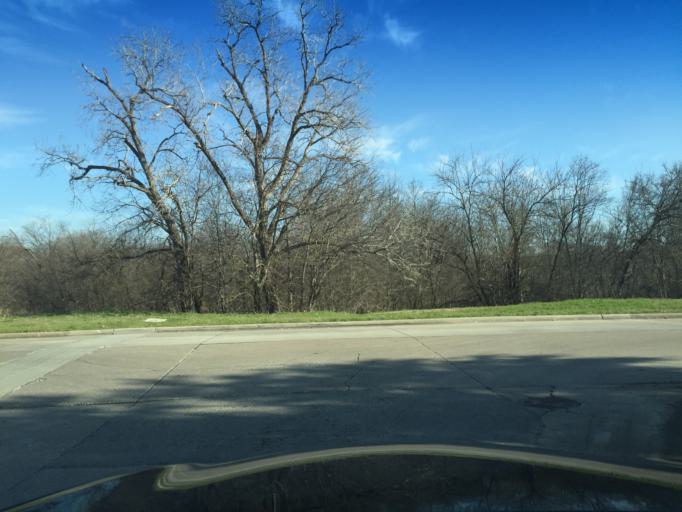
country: US
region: Texas
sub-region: Dallas County
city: Carrollton
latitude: 32.9980
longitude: -96.8943
